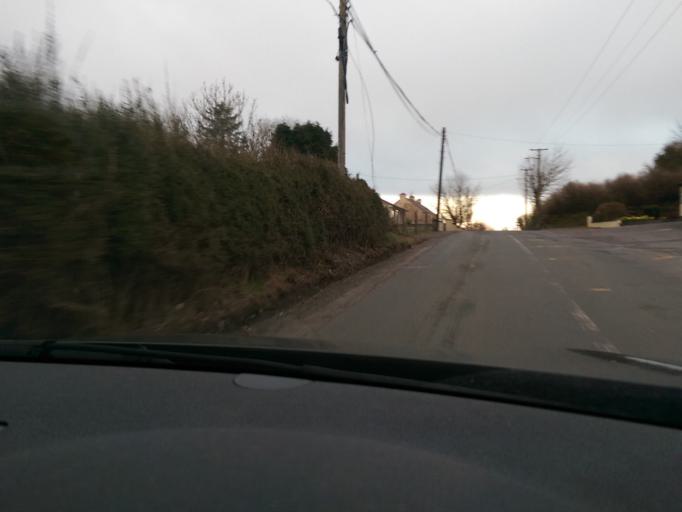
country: IE
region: Connaught
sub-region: Sligo
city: Ballymote
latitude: 53.9911
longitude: -8.5101
